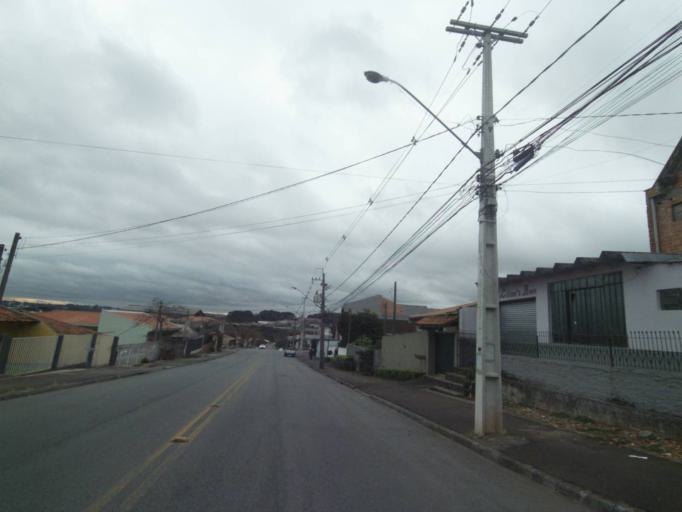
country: BR
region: Parana
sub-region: Curitiba
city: Curitiba
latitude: -25.5186
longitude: -49.3085
